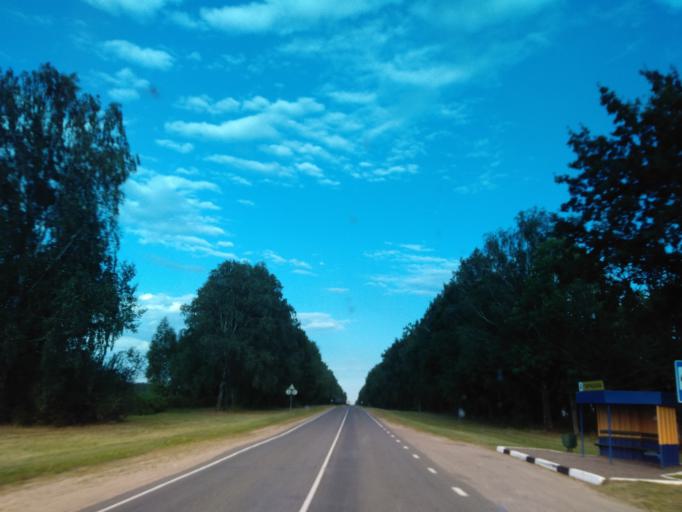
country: BY
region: Minsk
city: Uzda
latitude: 53.4266
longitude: 27.3617
